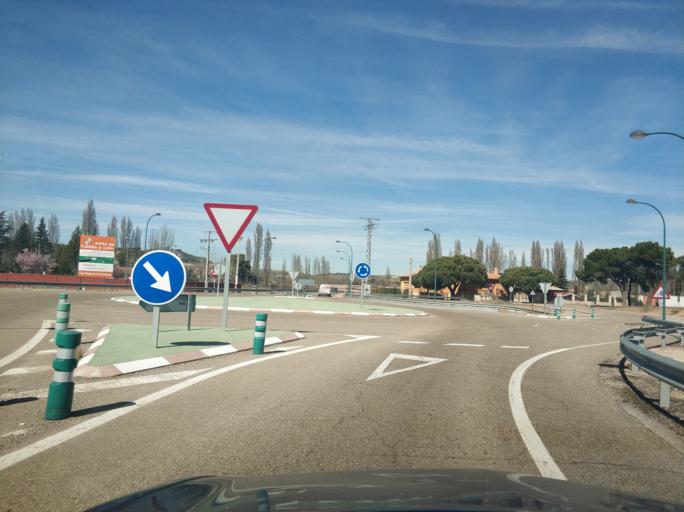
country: ES
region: Castille and Leon
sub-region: Provincia de Valladolid
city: Simancas
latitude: 41.5811
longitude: -4.8149
